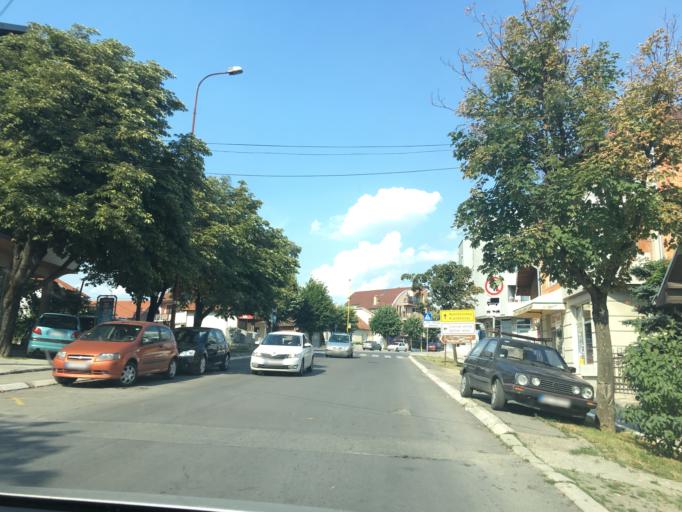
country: RS
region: Central Serbia
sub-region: Belgrade
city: Lazarevac
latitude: 44.3816
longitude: 20.2694
